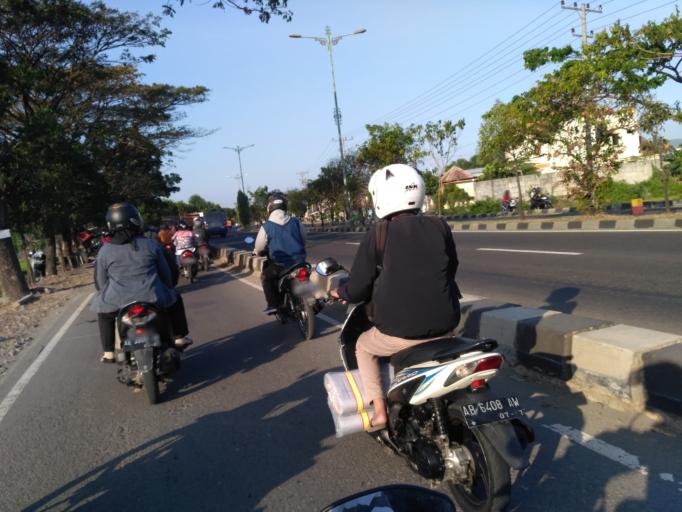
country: ID
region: Daerah Istimewa Yogyakarta
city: Sewon
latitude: -7.8343
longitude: 110.3848
